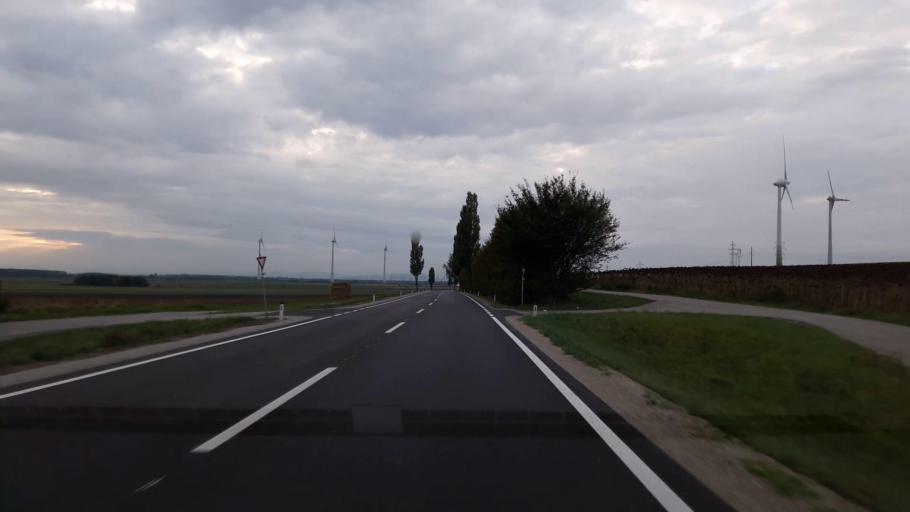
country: AT
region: Lower Austria
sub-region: Politischer Bezirk Bruck an der Leitha
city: Bruck an der Leitha
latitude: 48.0273
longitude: 16.7331
